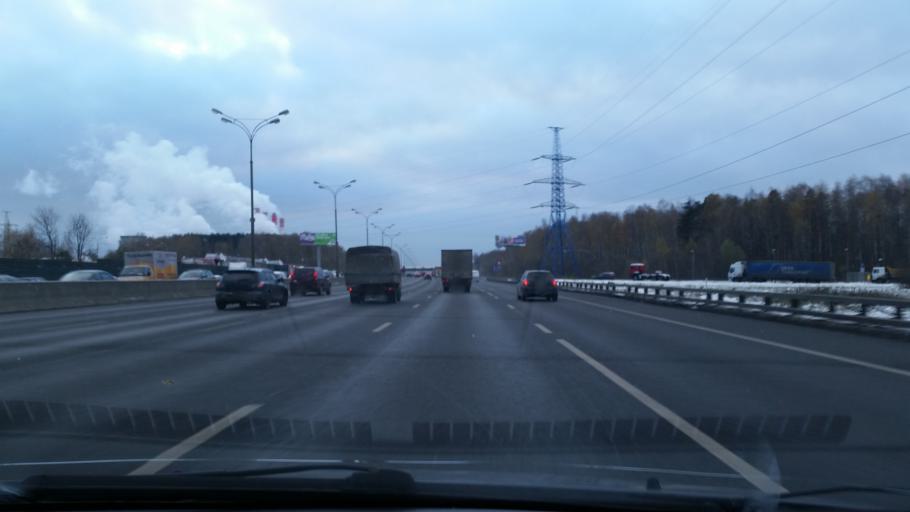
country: RU
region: Moscow
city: Vagonoremont
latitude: 55.9043
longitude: 37.5241
